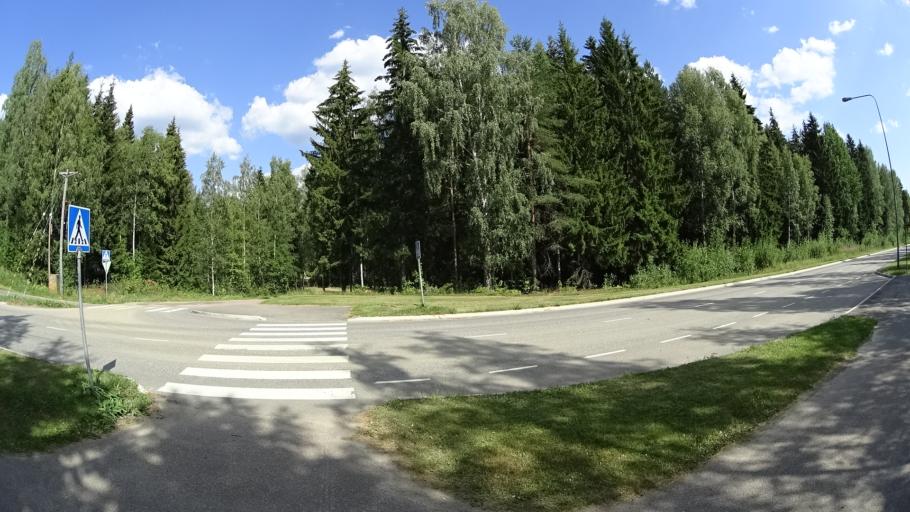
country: FI
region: Uusimaa
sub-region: Porvoo
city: Porvoo
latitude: 60.3923
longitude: 25.7054
